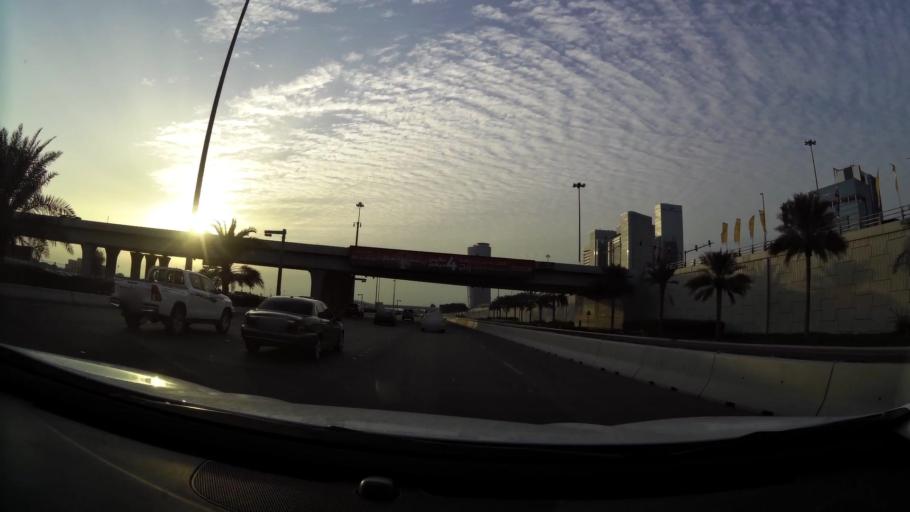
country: AE
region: Abu Dhabi
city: Abu Dhabi
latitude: 24.4153
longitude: 54.4439
